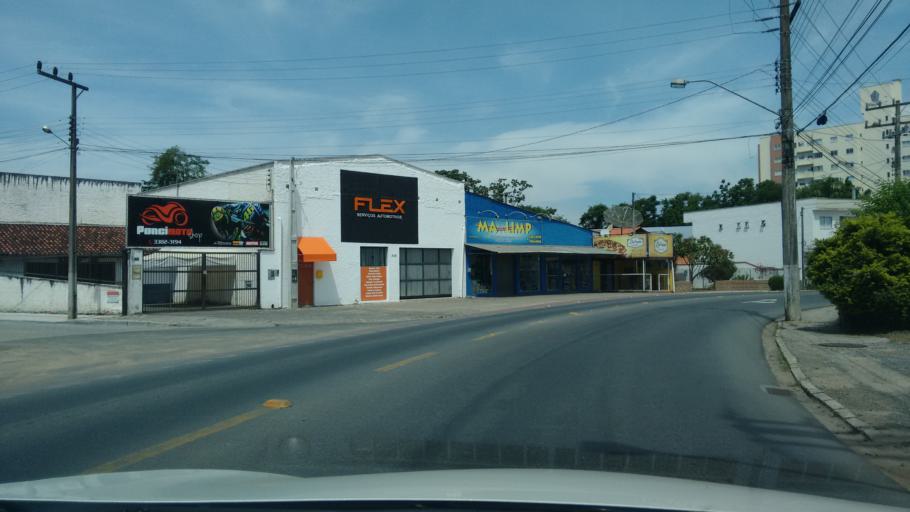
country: BR
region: Santa Catarina
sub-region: Timbo
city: Timbo
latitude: -26.8340
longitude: -49.2716
